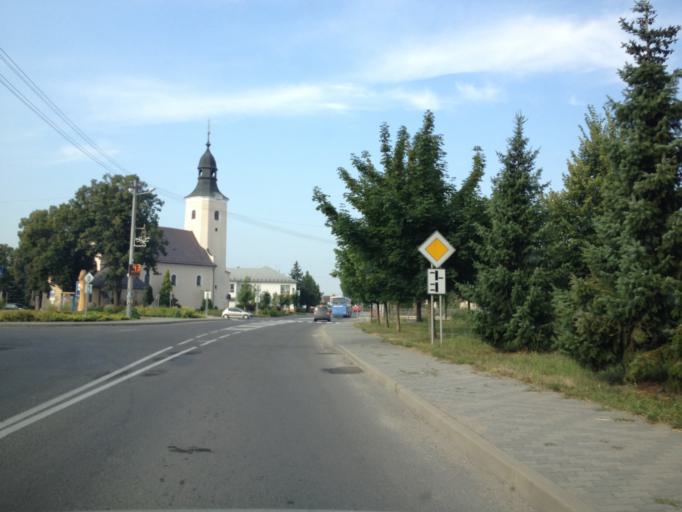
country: SK
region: Nitriansky
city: Puchov
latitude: 49.0659
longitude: 18.3282
